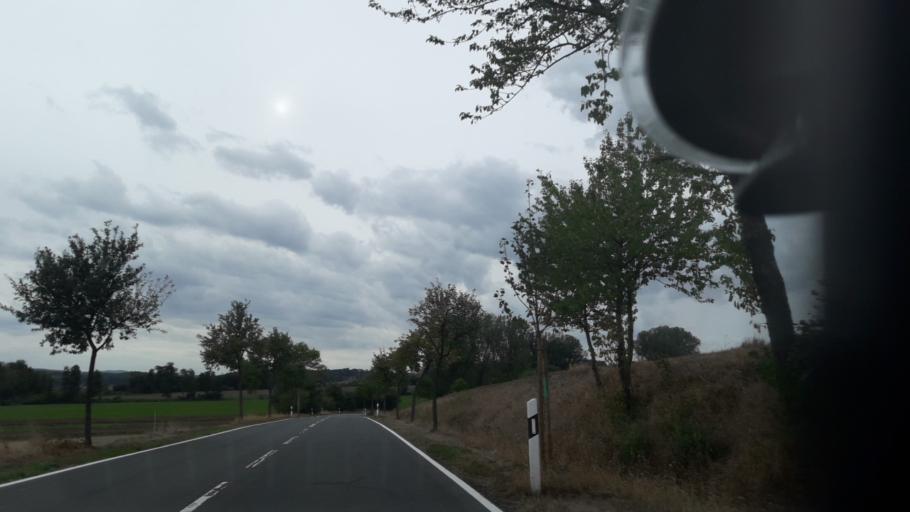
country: DE
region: Lower Saxony
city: Werlaburgdorf
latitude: 52.0493
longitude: 10.5205
